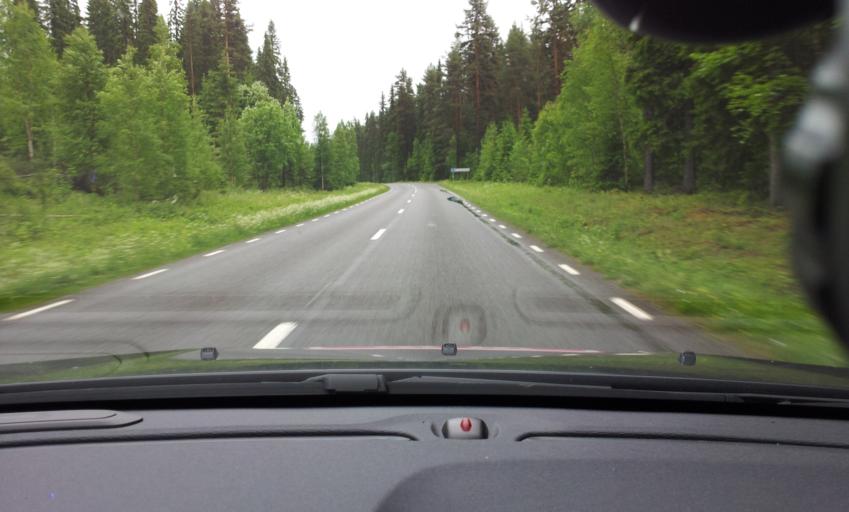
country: SE
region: Jaemtland
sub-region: Stroemsunds Kommun
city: Stroemsund
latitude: 63.4350
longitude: 15.4914
